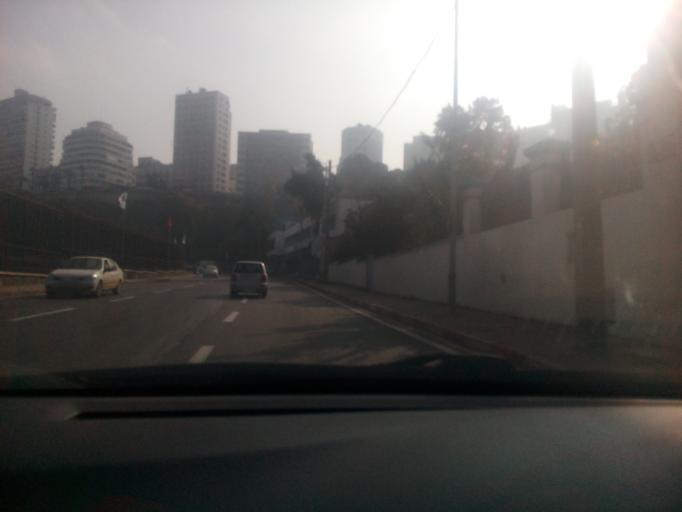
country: DZ
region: Oran
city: Oran
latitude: 35.7071
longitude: -0.6423
